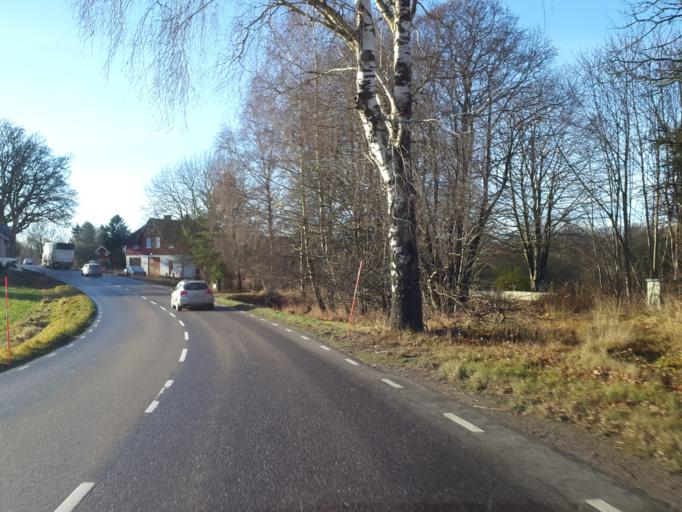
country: SE
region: Vaestra Goetaland
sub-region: Herrljunga Kommun
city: Herrljunga
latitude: 57.9946
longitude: 12.9313
